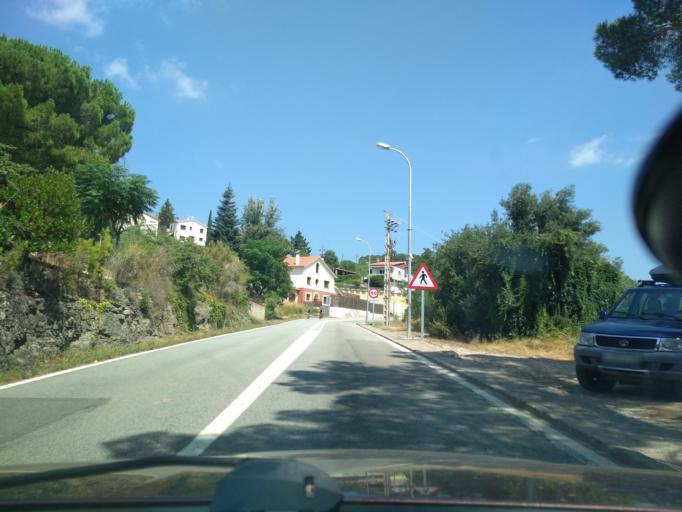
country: ES
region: Catalonia
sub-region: Provincia de Barcelona
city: Sant Feliu de Codines
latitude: 41.6905
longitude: 2.1698
